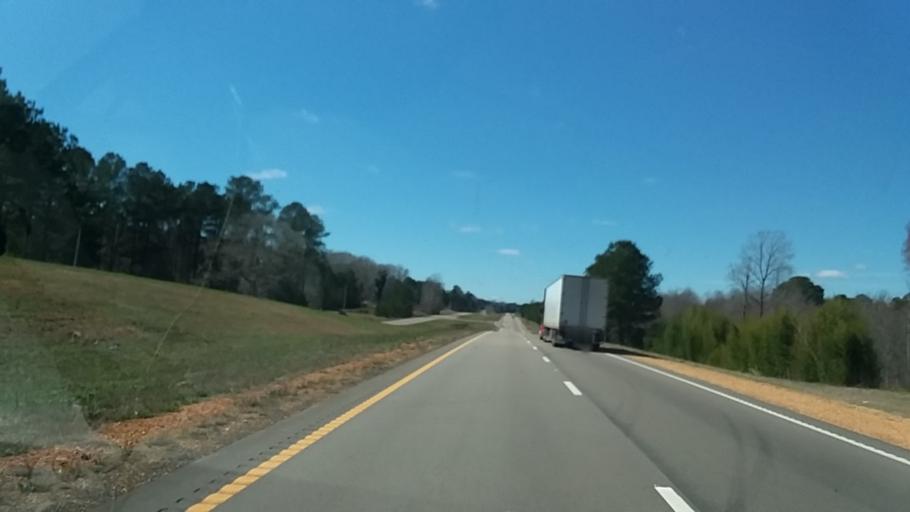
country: US
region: Mississippi
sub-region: Alcorn County
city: Farmington
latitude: 34.8590
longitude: -88.3965
